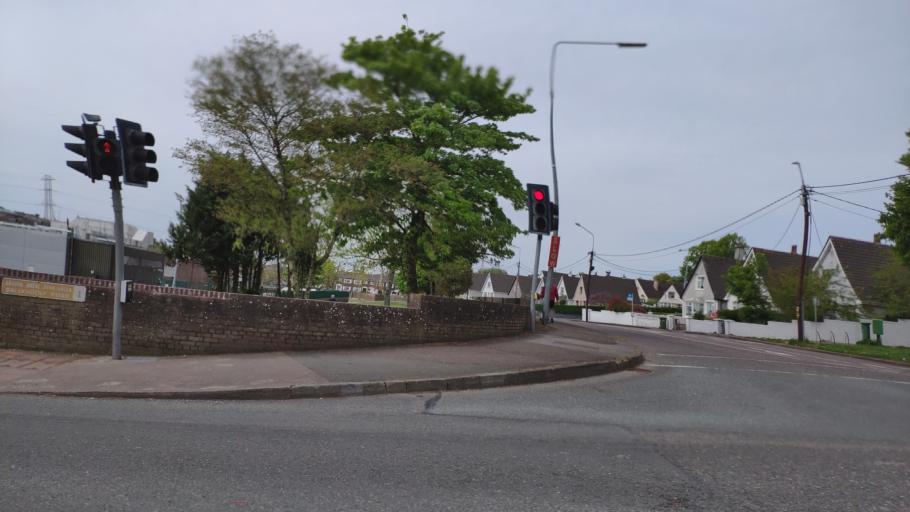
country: IE
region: Munster
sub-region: County Cork
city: Cork
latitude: 51.9171
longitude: -8.4467
